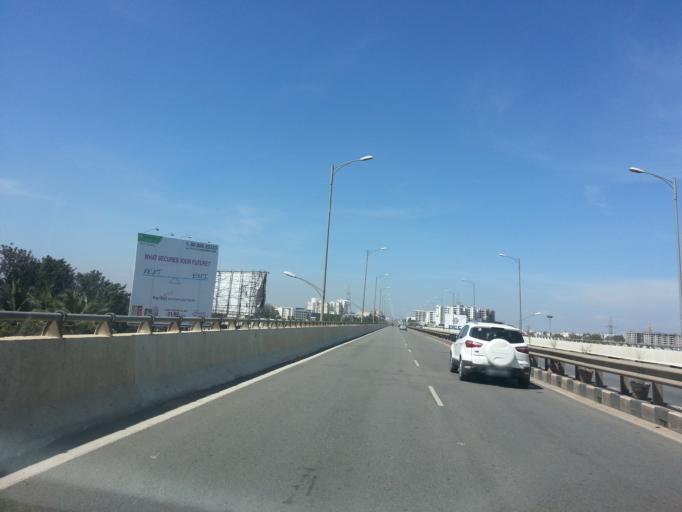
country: IN
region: Karnataka
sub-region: Bangalore Urban
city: Bangalore
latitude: 12.8556
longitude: 77.6646
